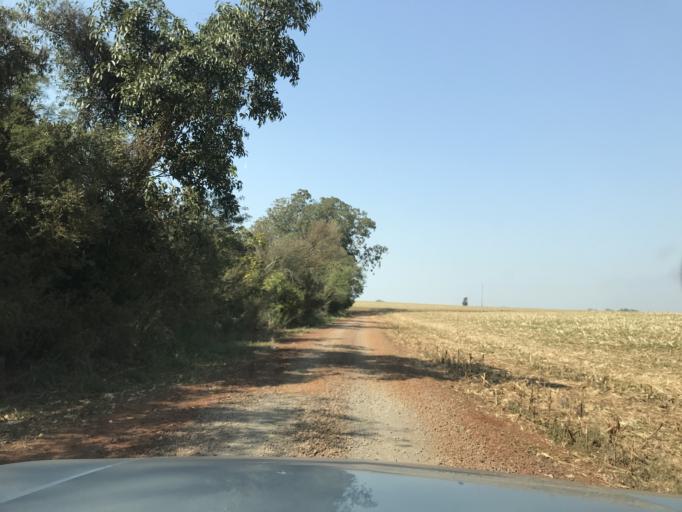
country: BR
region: Parana
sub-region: Palotina
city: Palotina
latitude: -24.2496
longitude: -53.7102
